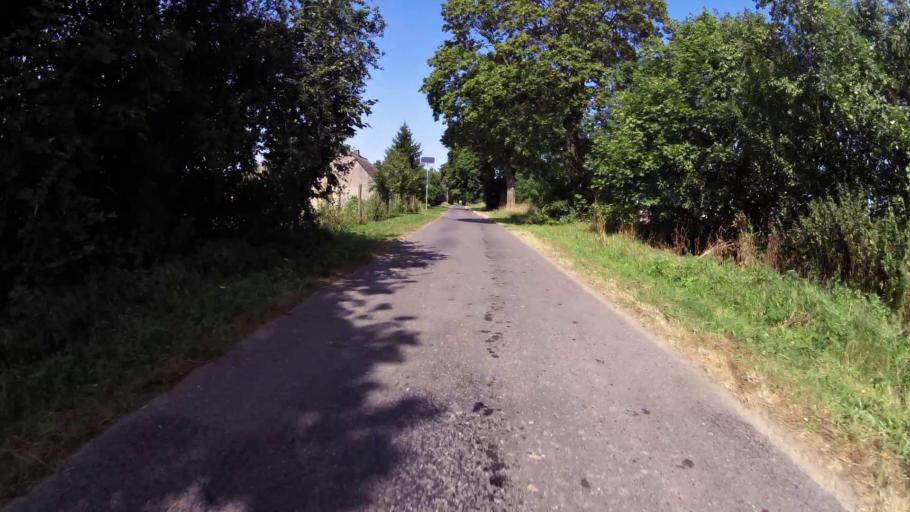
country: PL
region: West Pomeranian Voivodeship
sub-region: Powiat stargardzki
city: Suchan
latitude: 53.2932
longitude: 15.3643
